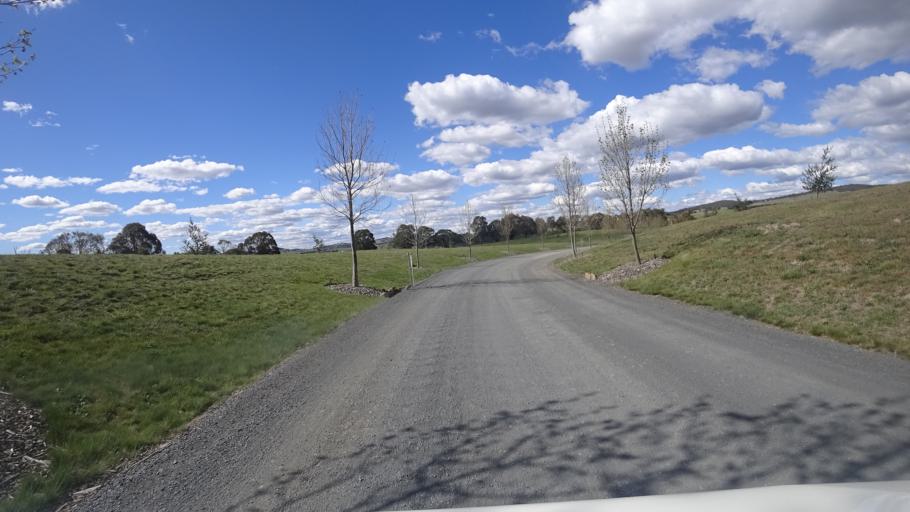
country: AU
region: New South Wales
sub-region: Oberon
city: Oberon
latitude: -33.6665
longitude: 149.7739
